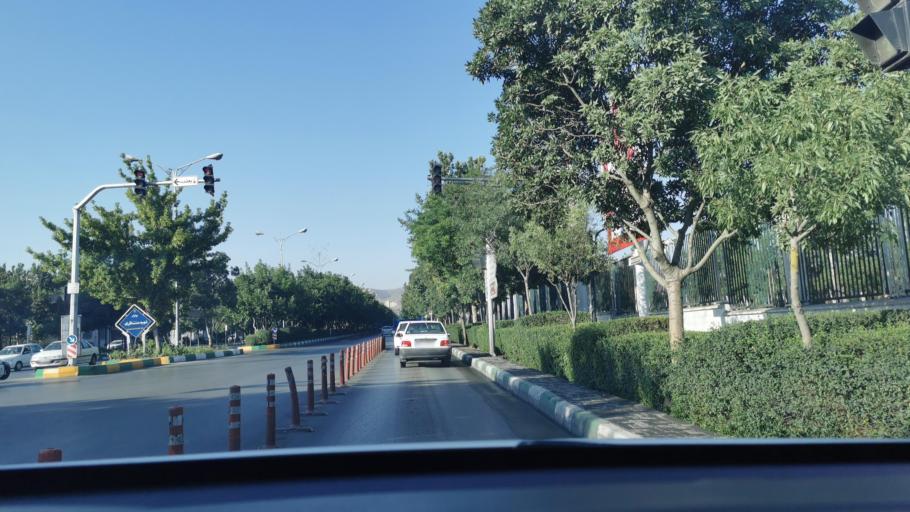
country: IR
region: Razavi Khorasan
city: Mashhad
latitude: 36.2931
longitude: 59.5597
